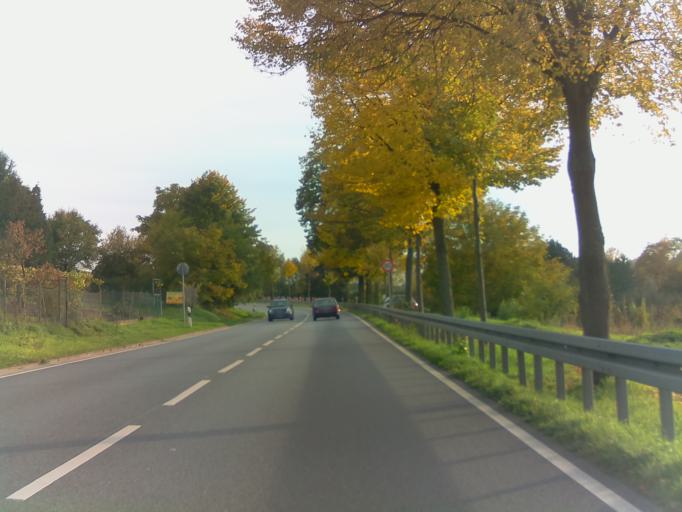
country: DE
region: Hesse
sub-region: Regierungsbezirk Darmstadt
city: Heppenheim an der Bergstrasse
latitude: 49.6288
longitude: 8.6416
